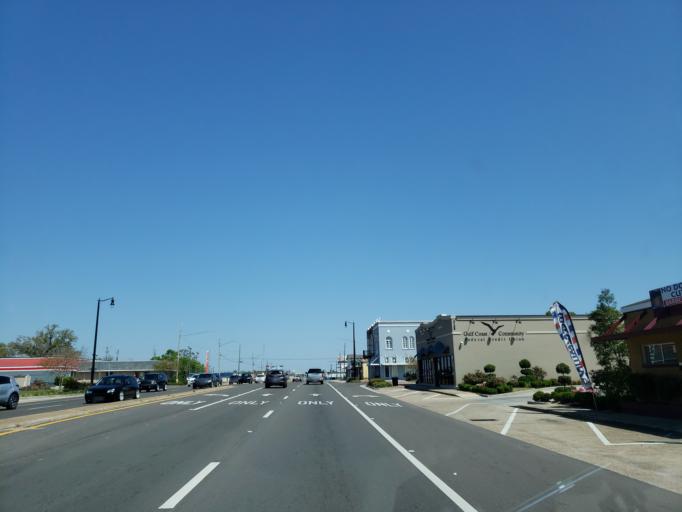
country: US
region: Mississippi
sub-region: Harrison County
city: Gulfport
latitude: 30.3760
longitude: -89.0929
